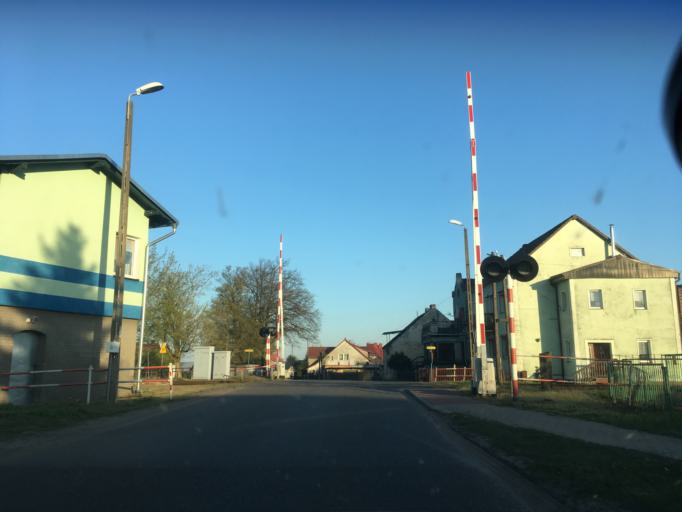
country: PL
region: Lubusz
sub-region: Powiat gorzowski
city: Bogdaniec
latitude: 52.6876
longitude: 15.0728
